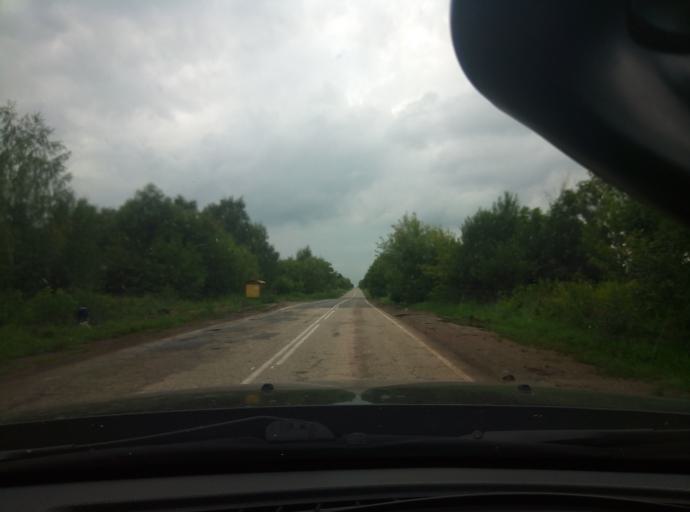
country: RU
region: Tula
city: Lomintsevskiy
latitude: 53.9578
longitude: 37.6999
